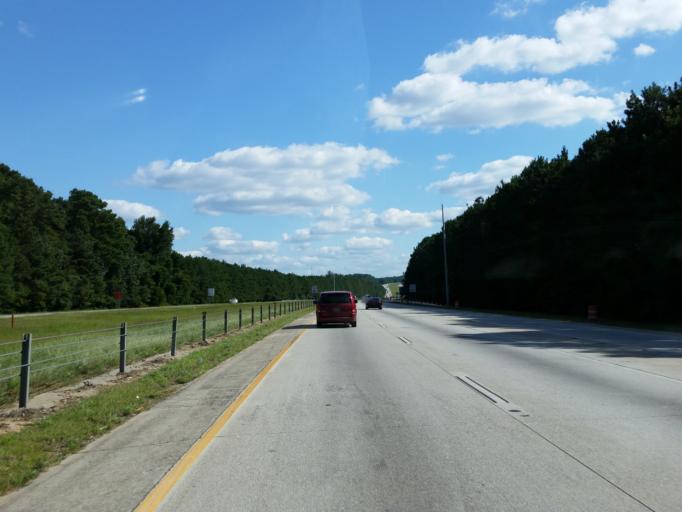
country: US
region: Georgia
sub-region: Henry County
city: Stockbridge
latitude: 33.5739
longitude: -84.2762
